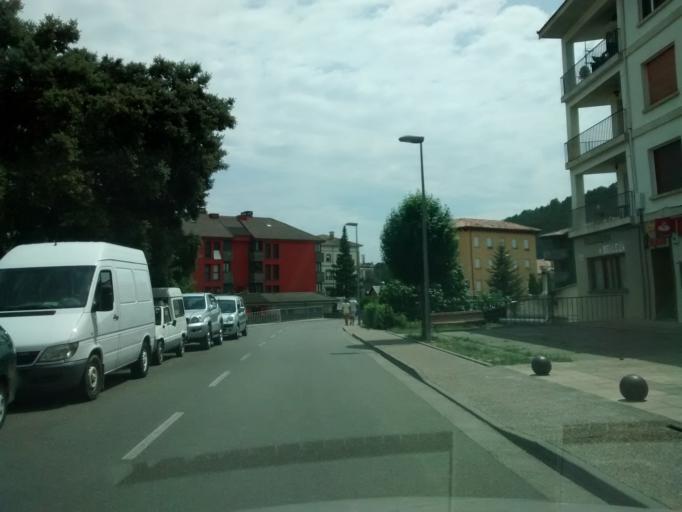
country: ES
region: Aragon
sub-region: Provincia de Huesca
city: Boltana
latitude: 42.4431
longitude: 0.0698
